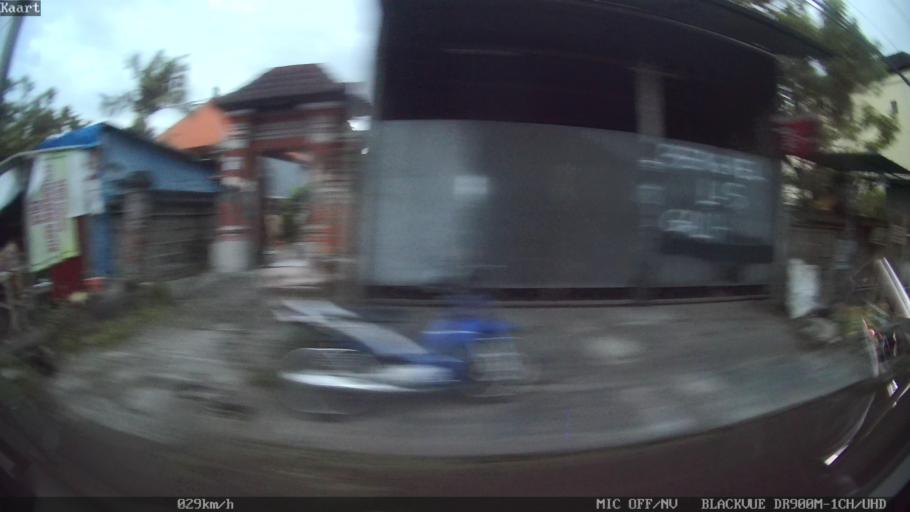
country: ID
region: Bali
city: Banjar Kertajiwa
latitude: -8.6399
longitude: 115.2670
